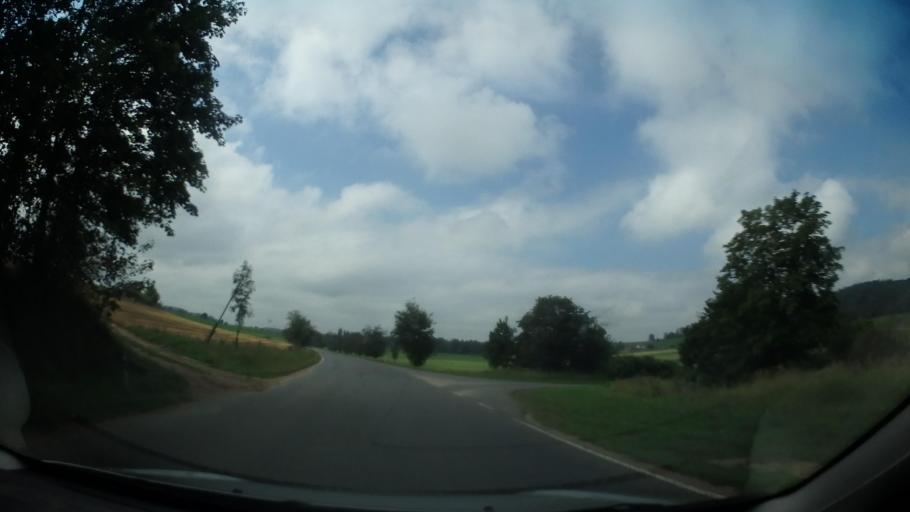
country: CZ
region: Central Bohemia
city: Sedlcany
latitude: 49.7007
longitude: 14.3634
